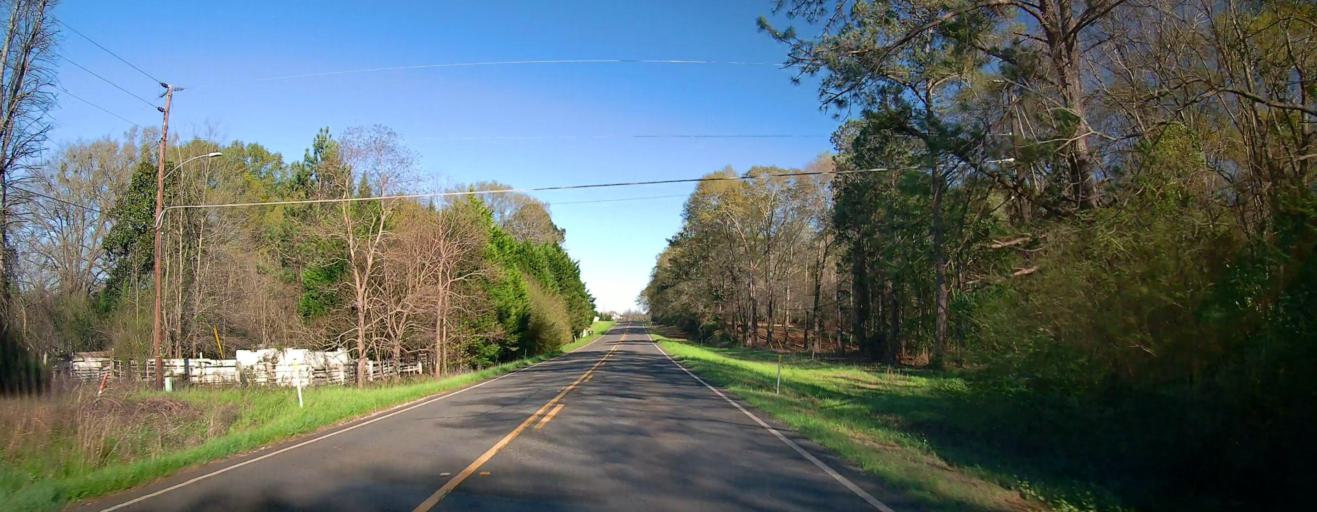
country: US
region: Georgia
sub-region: Macon County
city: Marshallville
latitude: 32.4561
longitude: -83.9284
